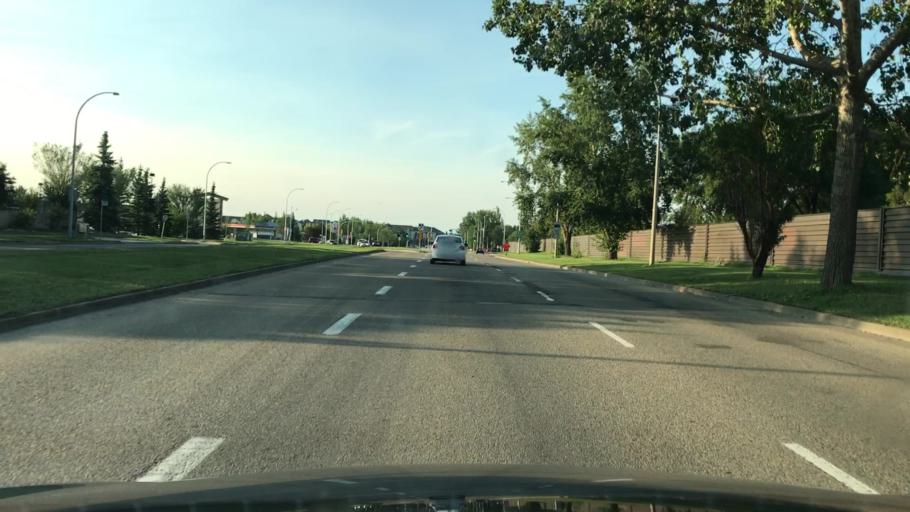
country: CA
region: Alberta
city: Beaumont
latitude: 53.4525
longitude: -113.4194
